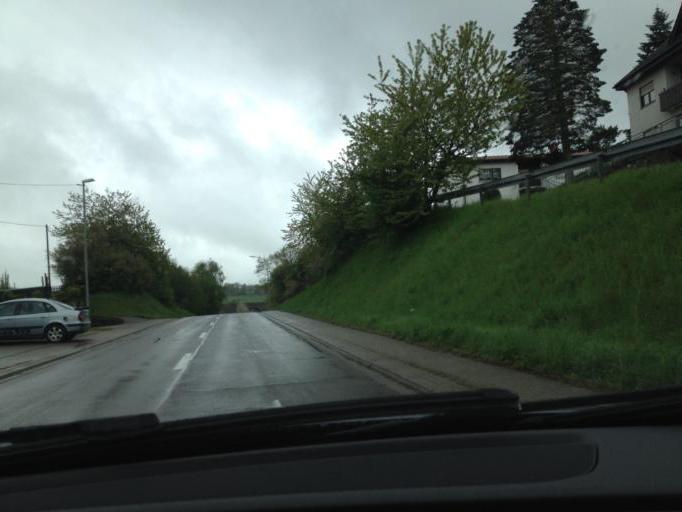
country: DE
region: Rheinland-Pfalz
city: Herchweiler
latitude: 49.5106
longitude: 7.2712
